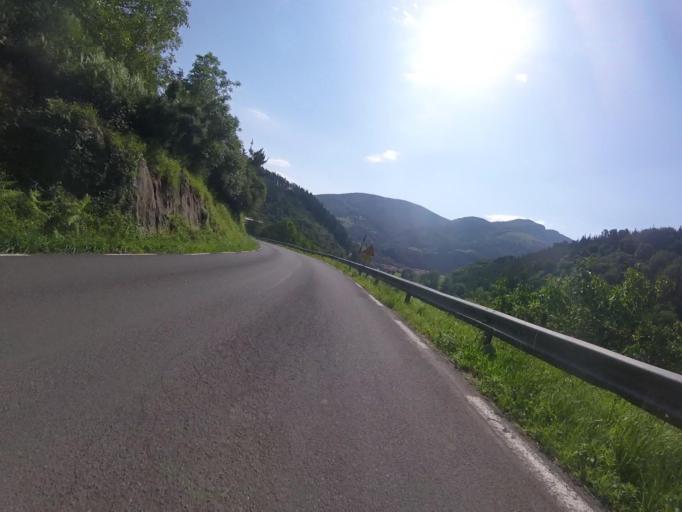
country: ES
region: Basque Country
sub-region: Provincia de Guipuzcoa
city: Hernialde
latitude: 43.1635
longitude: -2.0814
